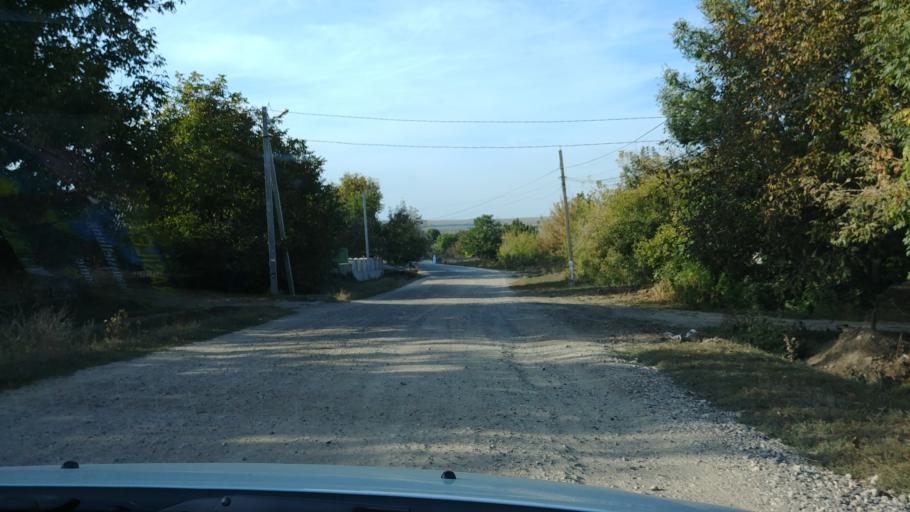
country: MD
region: Rezina
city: Rezina
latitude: 47.7479
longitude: 28.8848
